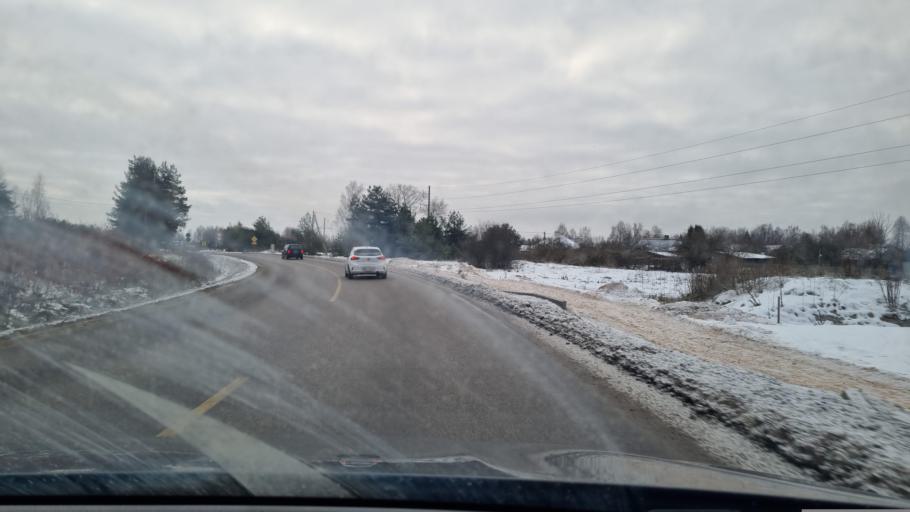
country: LV
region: Kekava
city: Balozi
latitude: 56.8814
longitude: 24.1544
